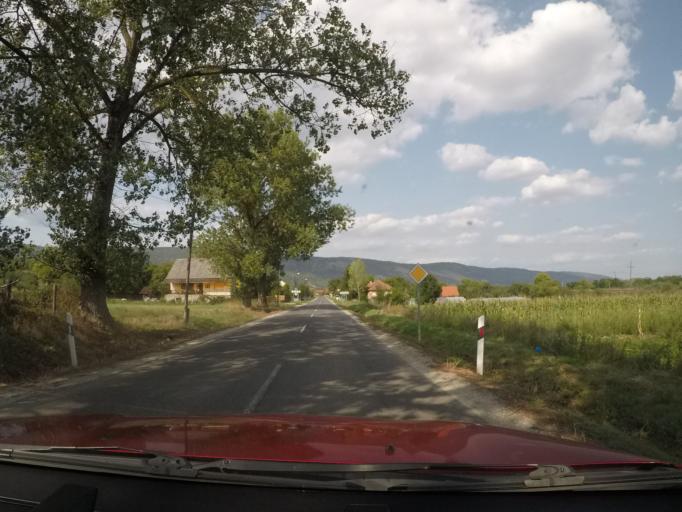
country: HU
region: Borsod-Abauj-Zemplen
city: Szendro
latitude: 48.5311
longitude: 20.7312
